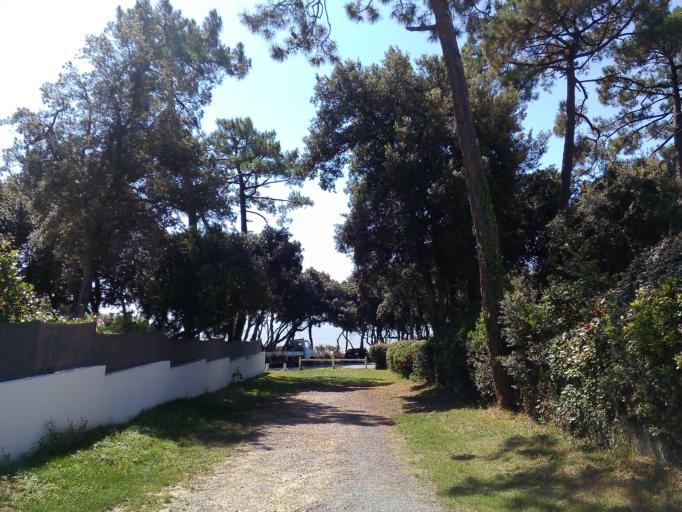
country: FR
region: Poitou-Charentes
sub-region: Departement de la Charente-Maritime
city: Saint-Palais-sur-Mer
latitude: 45.6353
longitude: -1.0723
